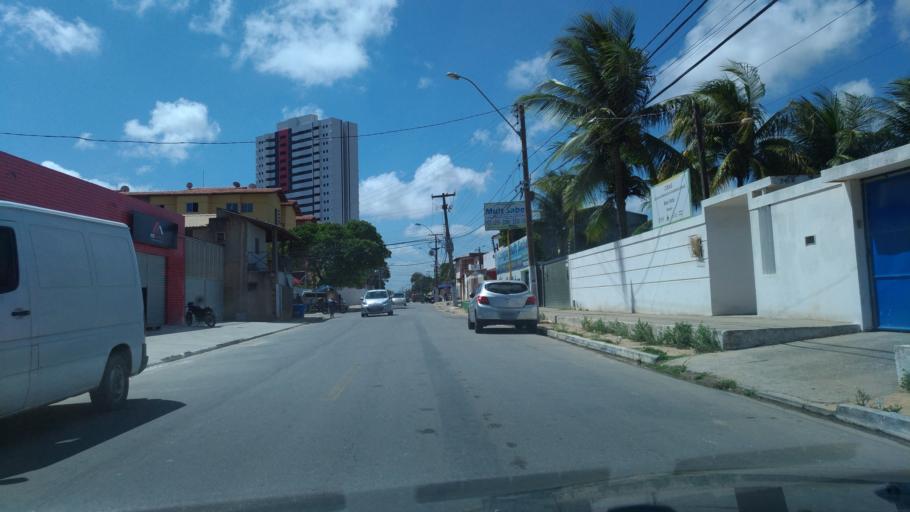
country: BR
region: Alagoas
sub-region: Maceio
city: Maceio
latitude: -9.6210
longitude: -35.7090
